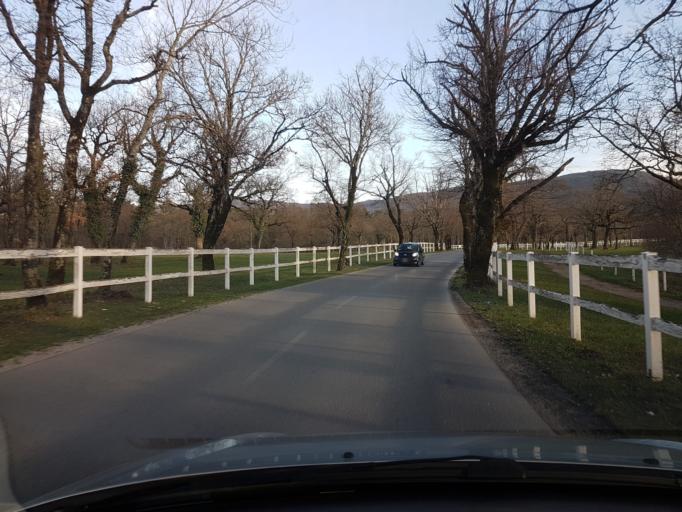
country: SI
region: Sezana
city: Sezana
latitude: 45.6644
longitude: 13.8904
